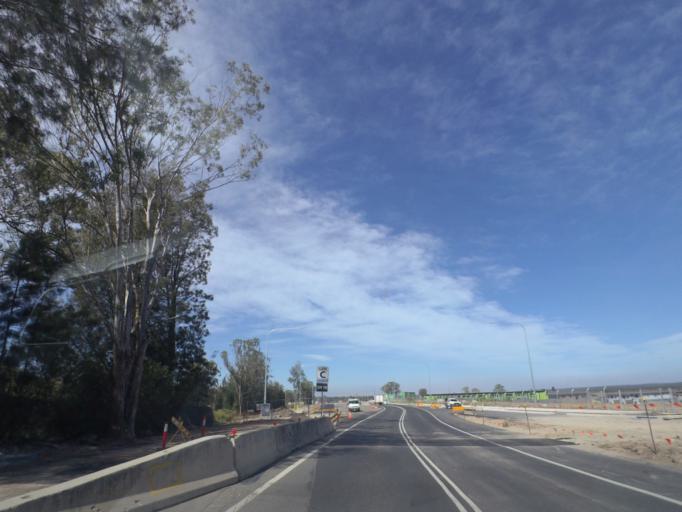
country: AU
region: New South Wales
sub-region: Campbelltown Municipality
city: Denham Court
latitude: -33.9755
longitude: 150.8538
